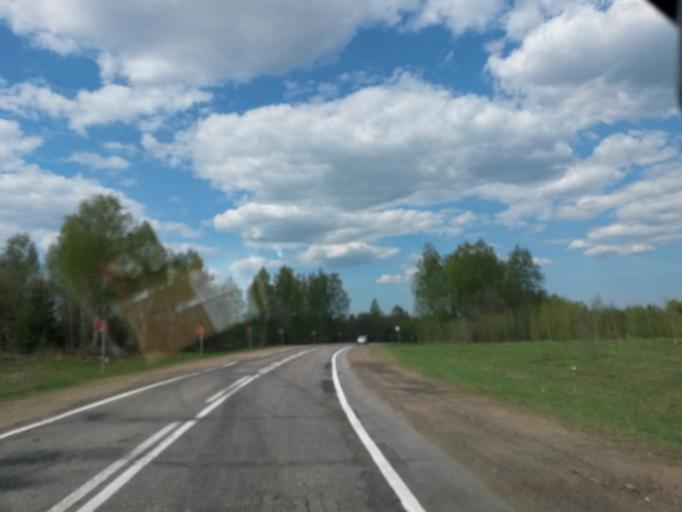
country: RU
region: Jaroslavl
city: Bol'shoye Selo
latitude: 57.6878
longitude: 39.1986
